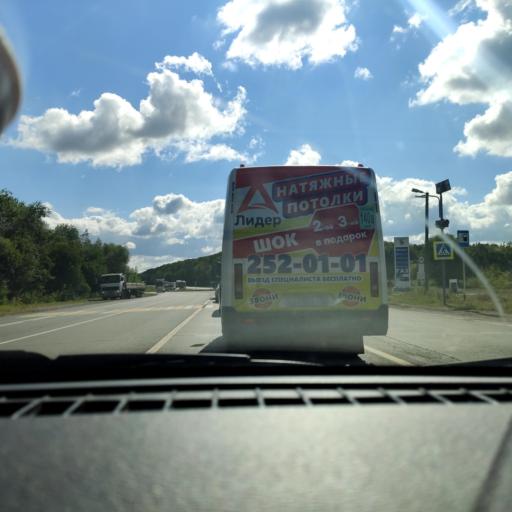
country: RU
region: Samara
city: Novokuybyshevsk
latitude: 52.9827
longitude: 49.8758
